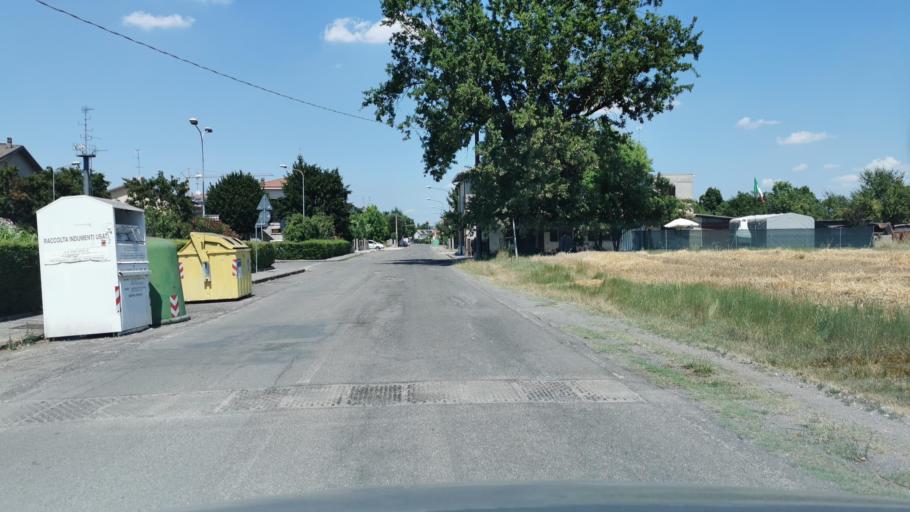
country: IT
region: Emilia-Romagna
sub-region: Provincia di Modena
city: Fossoli
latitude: 44.8174
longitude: 10.8960
